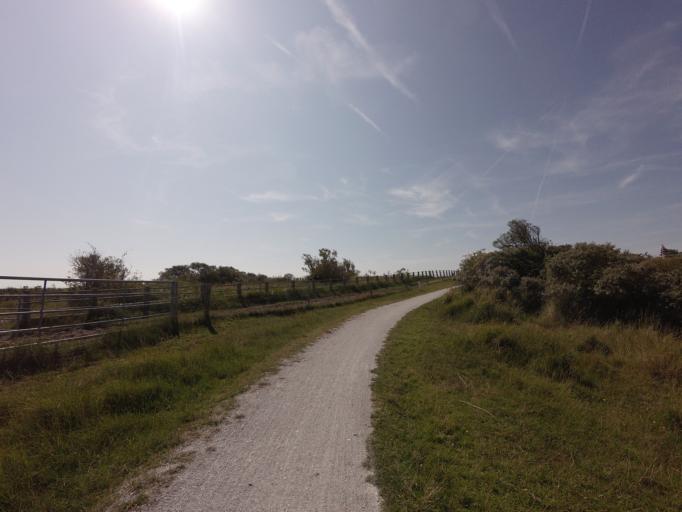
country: NL
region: Friesland
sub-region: Gemeente Schiermonnikoog
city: Schiermonnikoog
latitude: 53.4808
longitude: 6.2111
